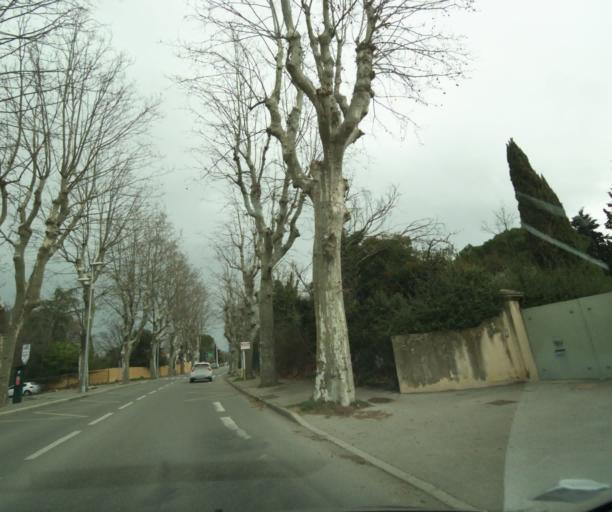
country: FR
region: Provence-Alpes-Cote d'Azur
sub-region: Departement des Bouches-du-Rhone
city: Aix-en-Provence
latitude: 43.5561
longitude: 5.4598
